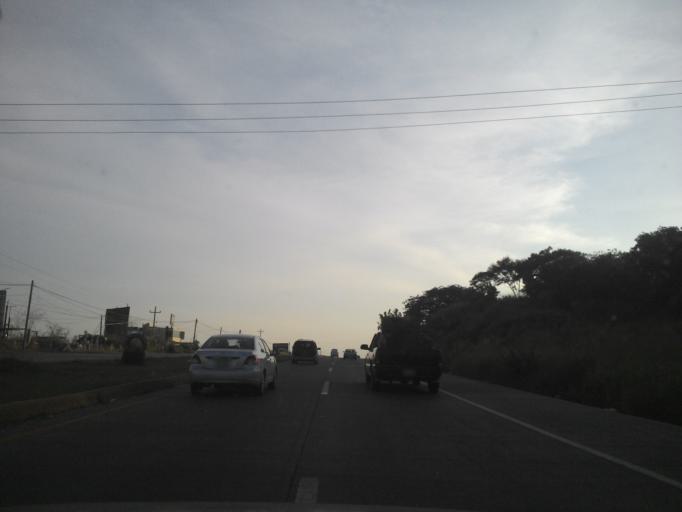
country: MX
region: Jalisco
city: Zapotlanejo
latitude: 20.6055
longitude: -103.0921
